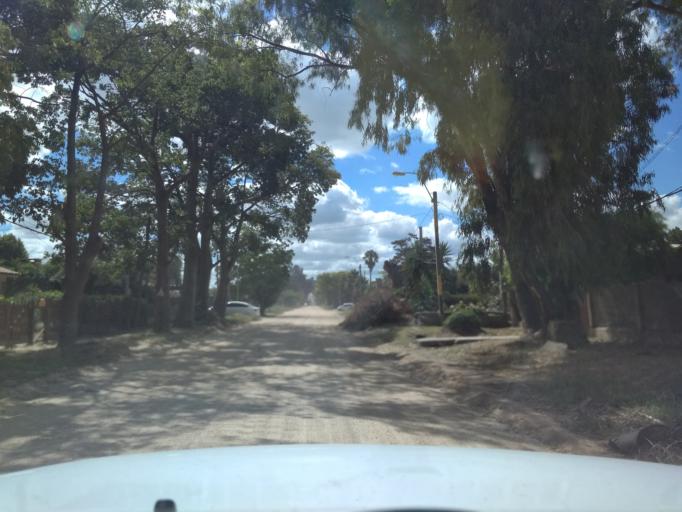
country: UY
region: Canelones
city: Barra de Carrasco
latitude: -34.8342
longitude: -55.9870
